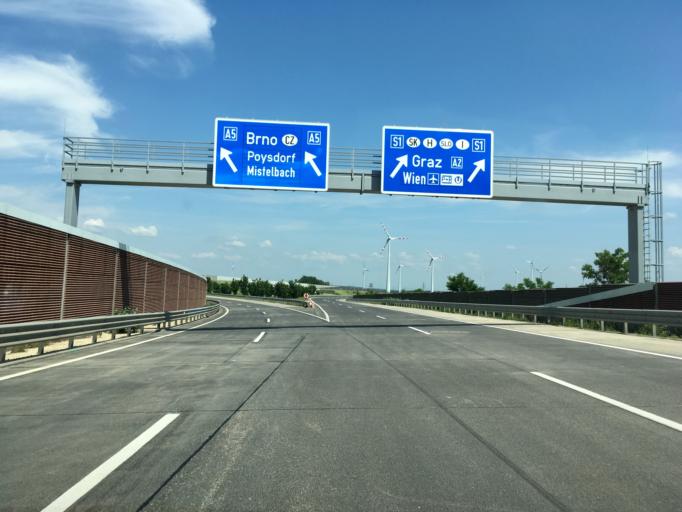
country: AT
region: Lower Austria
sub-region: Politischer Bezirk Mistelbach
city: Grossebersdorf
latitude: 48.3467
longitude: 16.4775
